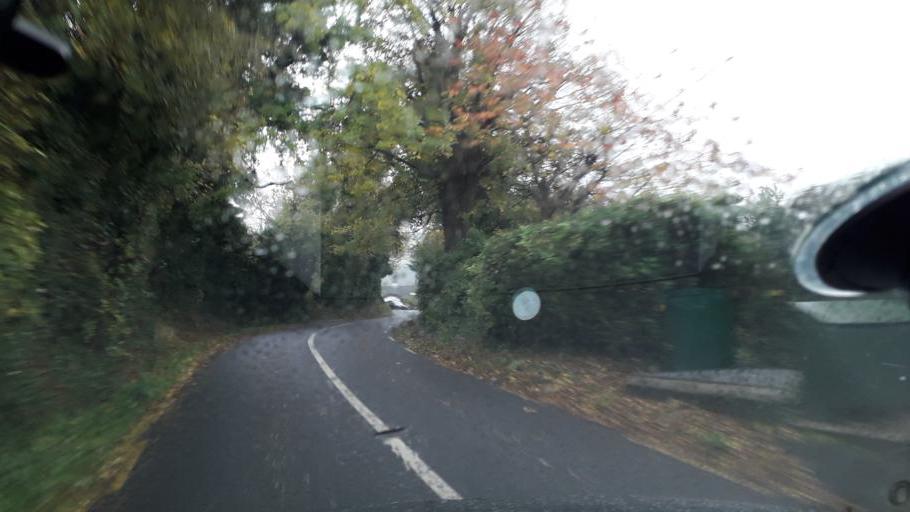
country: IE
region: Leinster
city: Ballyboden
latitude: 53.2525
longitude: -6.3026
